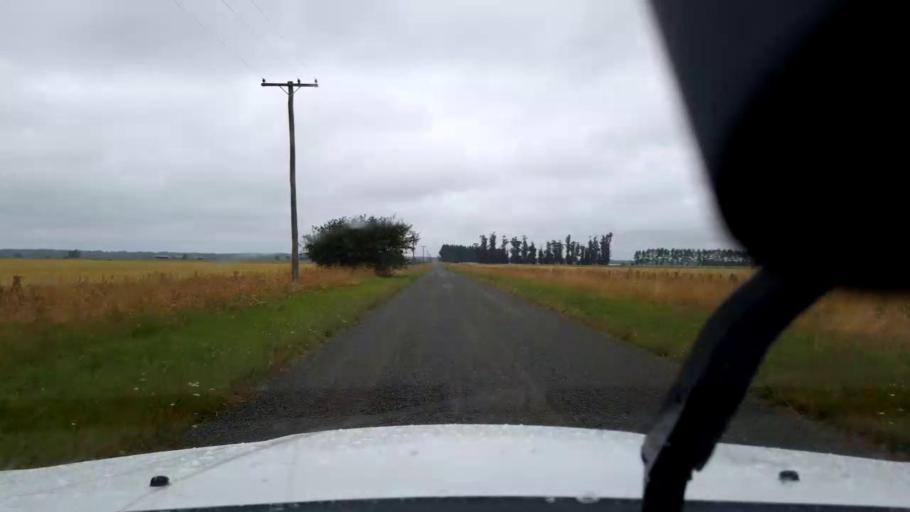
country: NZ
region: Canterbury
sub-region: Timaru District
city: Pleasant Point
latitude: -44.2327
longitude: 171.2026
